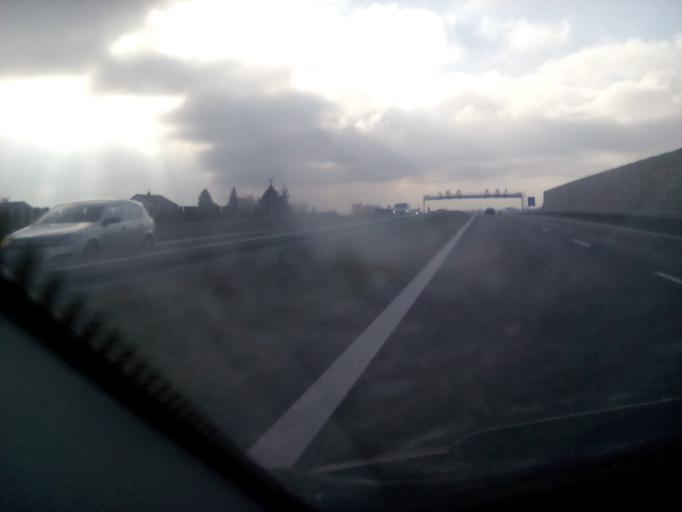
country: PL
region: Masovian Voivodeship
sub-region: Powiat bialobrzeski
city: Promna
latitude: 51.7083
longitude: 20.9263
